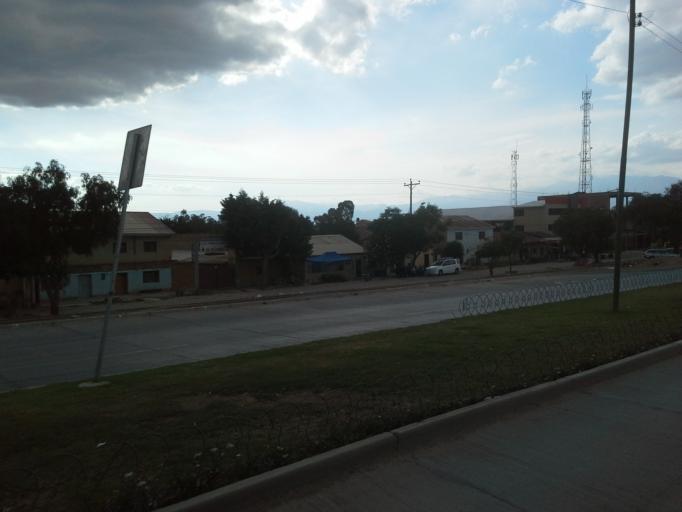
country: BO
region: Cochabamba
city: Cochabamba
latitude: -17.4578
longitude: -66.1244
